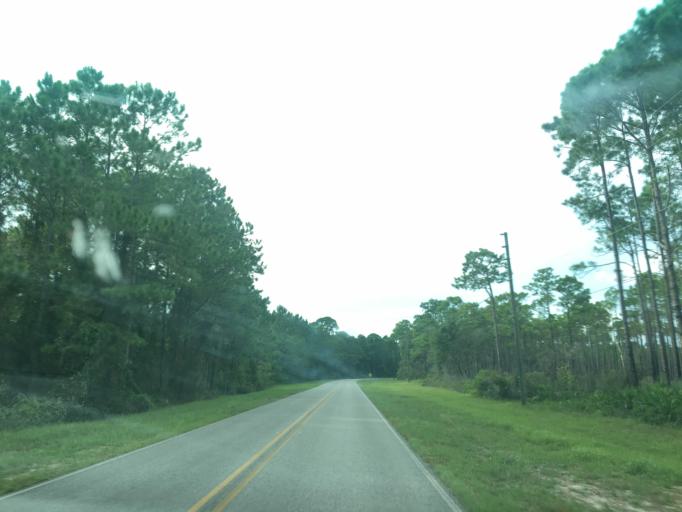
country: US
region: Florida
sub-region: Wakulla County
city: Crawfordville
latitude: 29.9270
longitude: -84.3769
